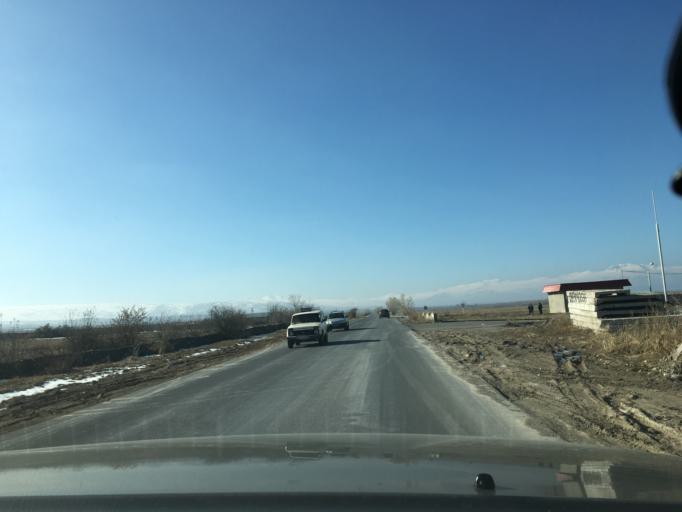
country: AM
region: Geghark'unik'i Marz
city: Vardenik
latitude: 40.1509
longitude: 45.4166
